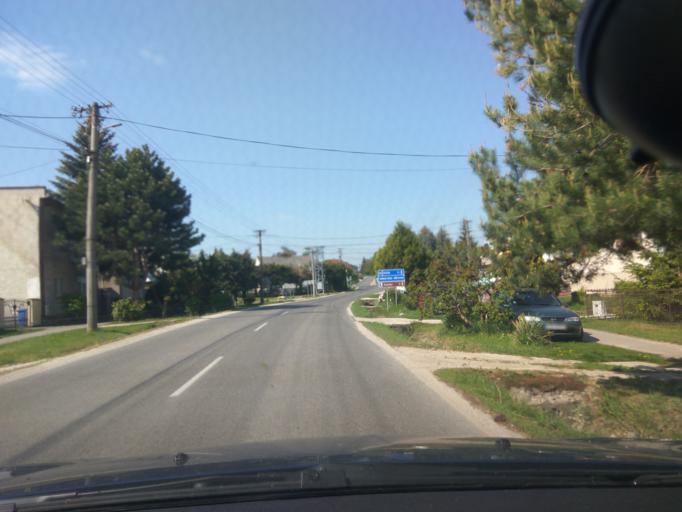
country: SK
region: Nitriansky
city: Brezova pod Bradlom
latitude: 48.5459
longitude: 17.5917
